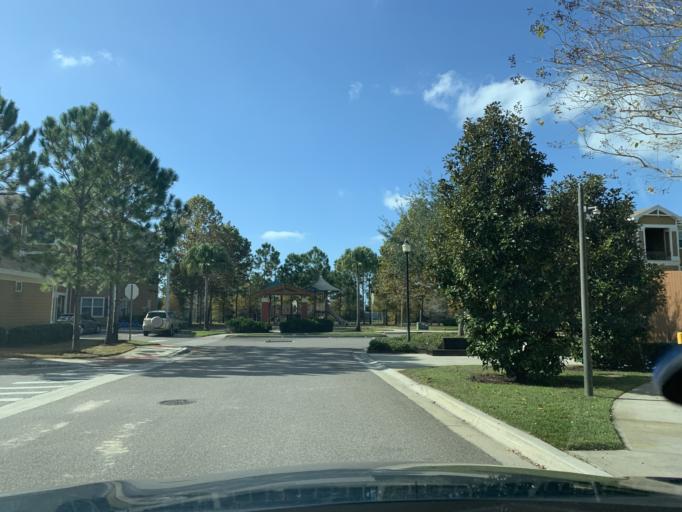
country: US
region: Florida
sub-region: Pinellas County
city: Belleair
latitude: 27.9328
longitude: -82.7977
